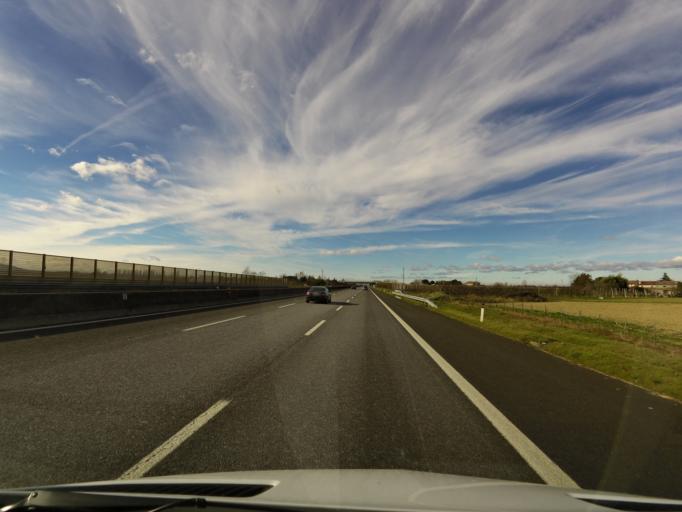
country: IT
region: Emilia-Romagna
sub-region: Forli-Cesena
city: Cesena
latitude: 44.1839
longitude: 12.2530
